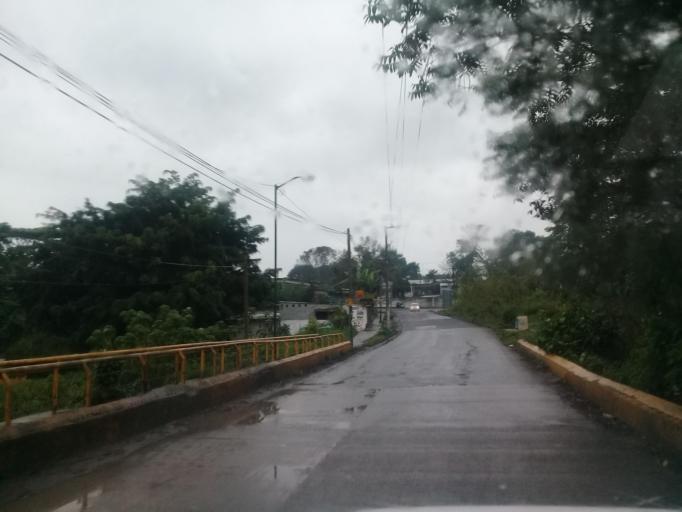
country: MX
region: Veracruz
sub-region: Cordoba
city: San Jose de Tapia
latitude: 18.8472
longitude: -96.9518
